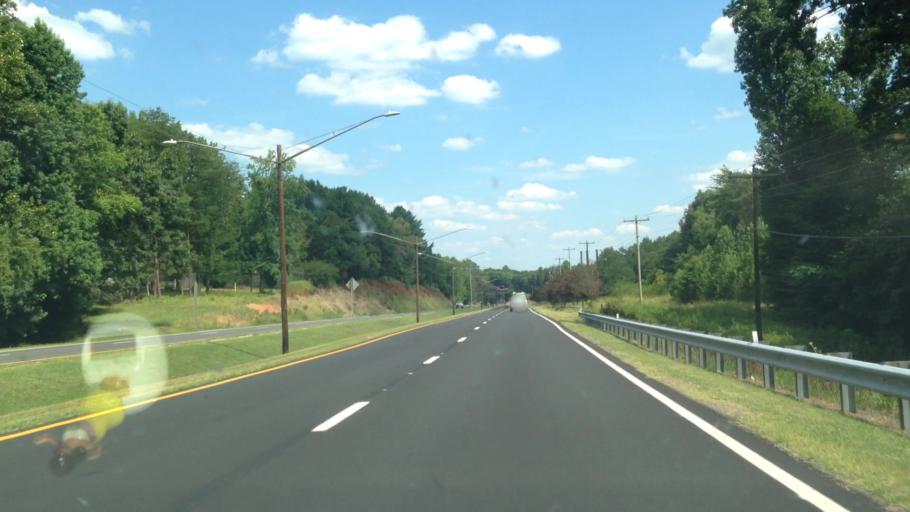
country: US
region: Virginia
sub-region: City of Danville
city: Danville
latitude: 36.5848
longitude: -79.4467
